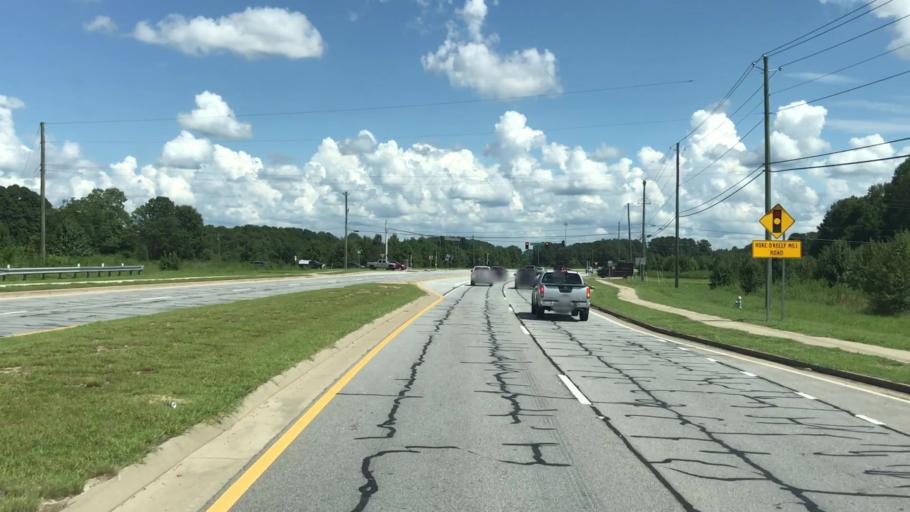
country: US
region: Georgia
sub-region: Walton County
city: Loganville
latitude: 33.8682
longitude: -83.9122
